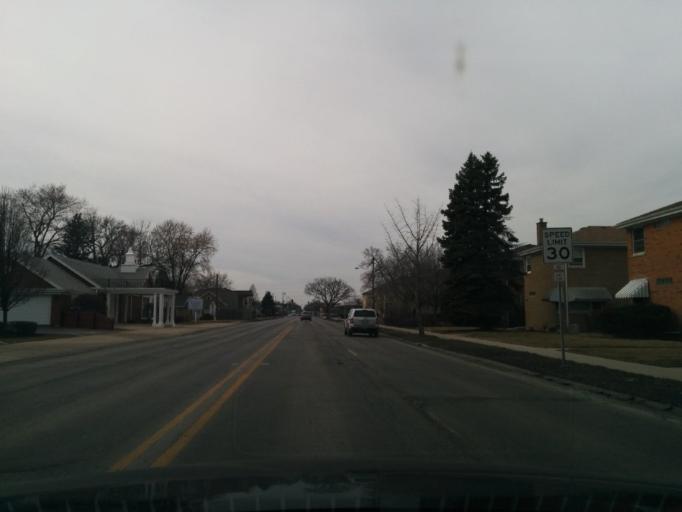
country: US
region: Illinois
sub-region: Cook County
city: La Grange Park
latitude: 41.8348
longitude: -87.8581
